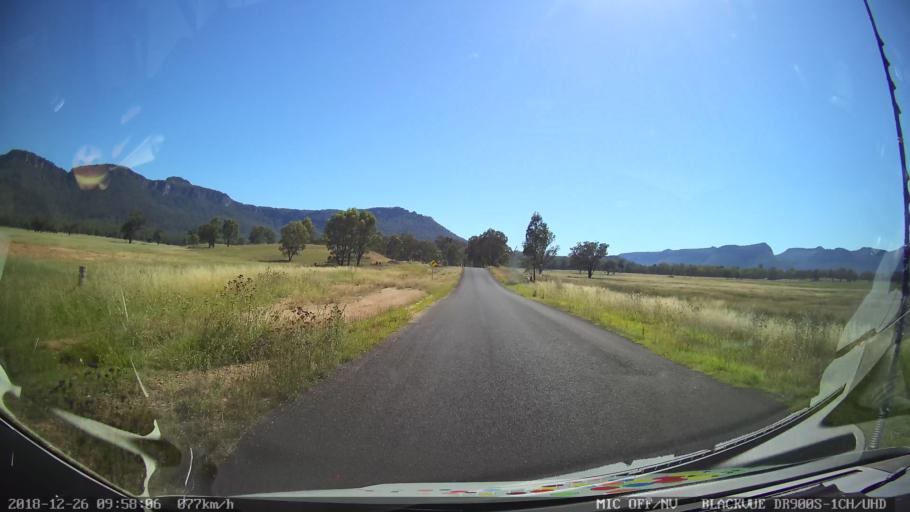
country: AU
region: New South Wales
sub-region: Mid-Western Regional
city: Kandos
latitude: -33.0394
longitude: 150.2010
